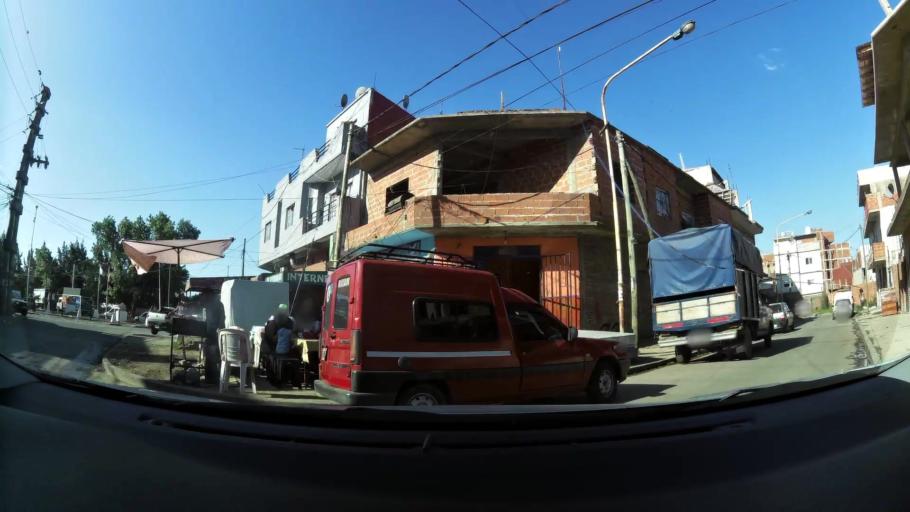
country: AR
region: Buenos Aires F.D.
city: Villa Lugano
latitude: -34.7008
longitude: -58.4822
